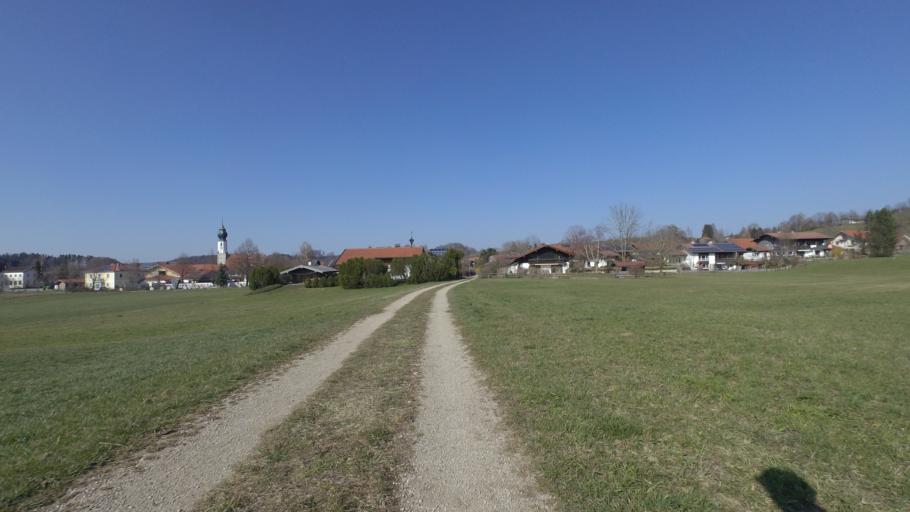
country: DE
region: Bavaria
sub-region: Upper Bavaria
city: Vachendorf
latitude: 47.8710
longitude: 12.5900
